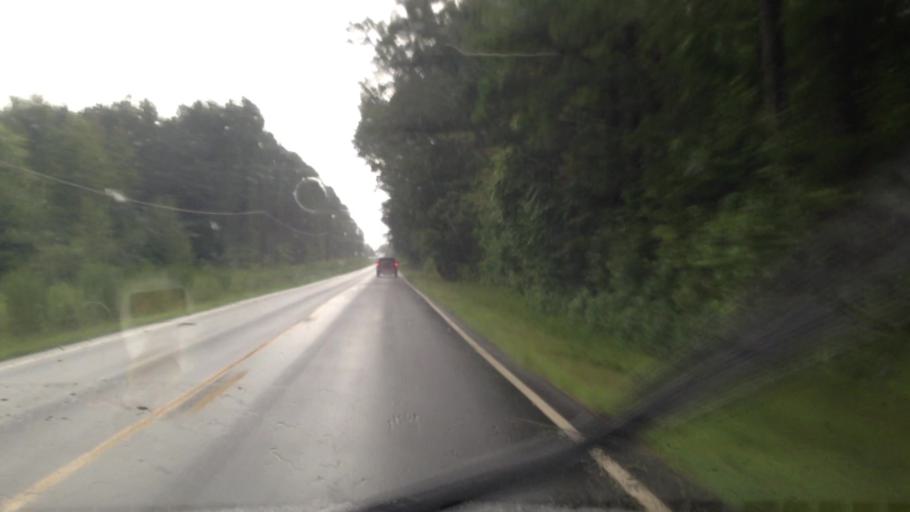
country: US
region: North Carolina
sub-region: Rockingham County
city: Reidsville
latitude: 36.2755
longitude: -79.7362
